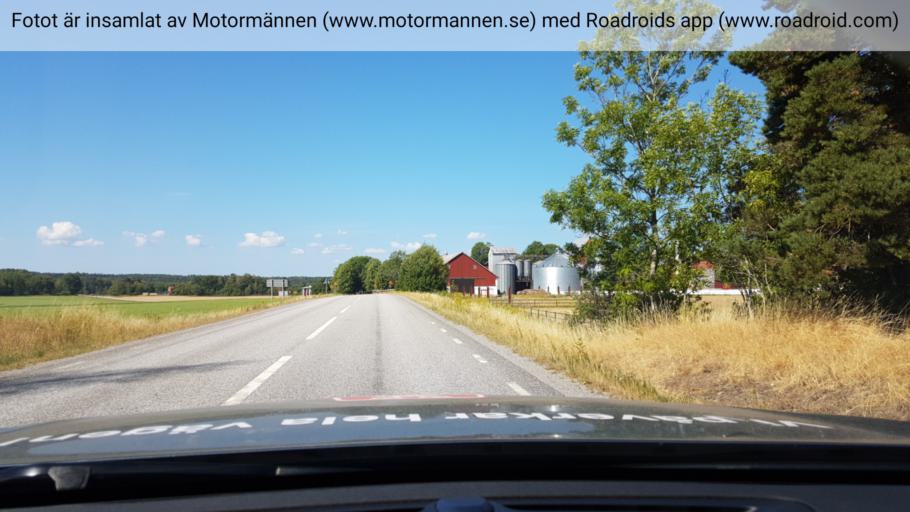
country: SE
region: Stockholm
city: Stenhamra
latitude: 59.3984
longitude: 17.5563
